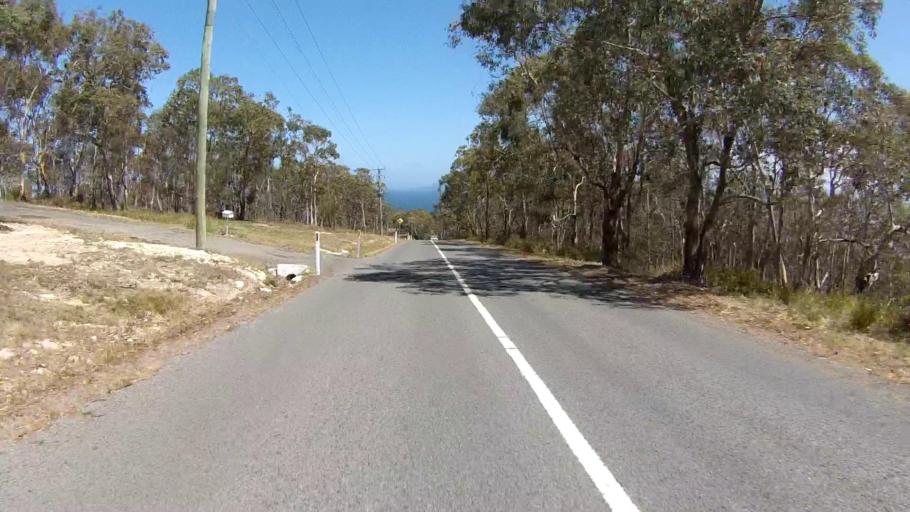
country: AU
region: Tasmania
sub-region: Clarence
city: Sandford
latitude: -43.0200
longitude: 147.4812
